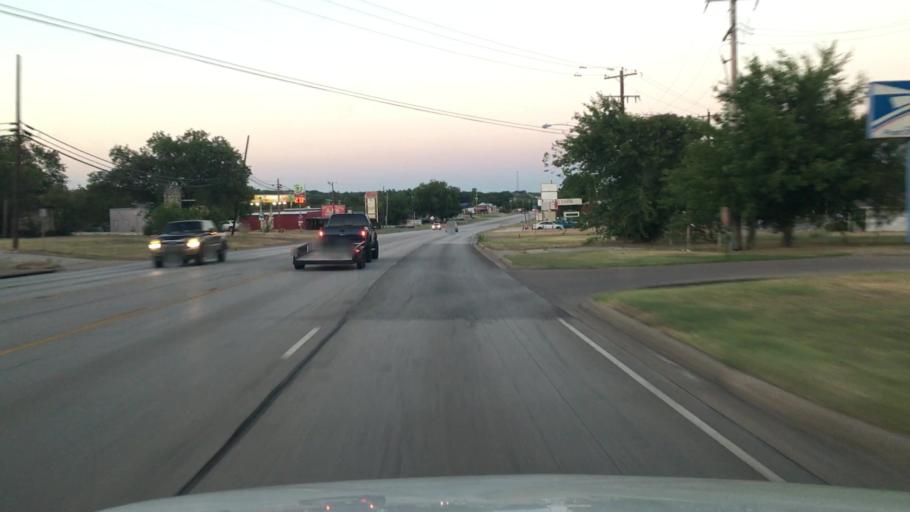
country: US
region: Texas
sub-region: Somervell County
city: Glen Rose
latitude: 32.2395
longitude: -97.7547
